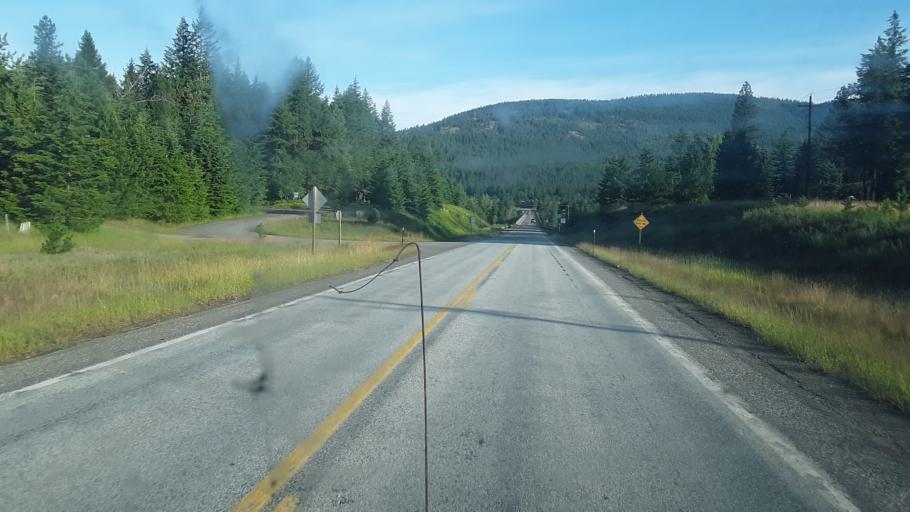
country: US
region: Idaho
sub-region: Boundary County
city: Bonners Ferry
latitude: 48.7257
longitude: -116.1739
